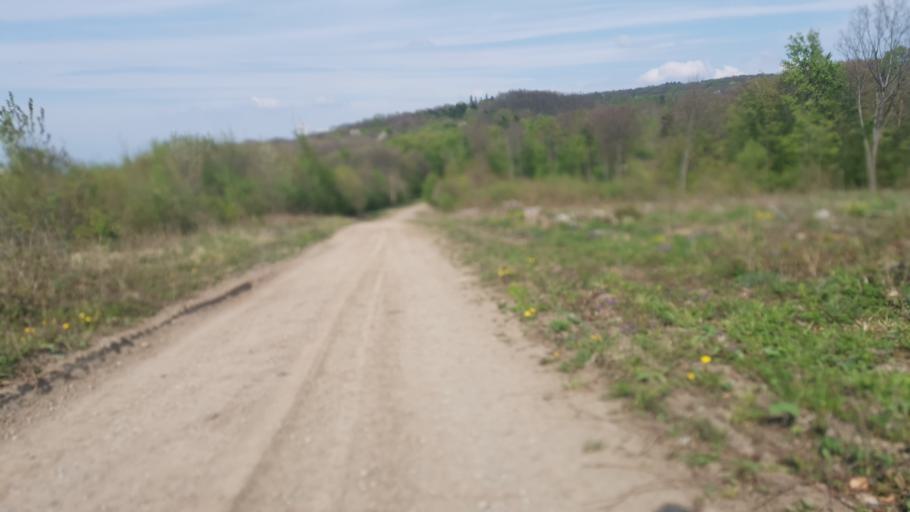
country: SK
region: Trnavsky
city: Smolenice
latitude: 48.5686
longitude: 17.3625
